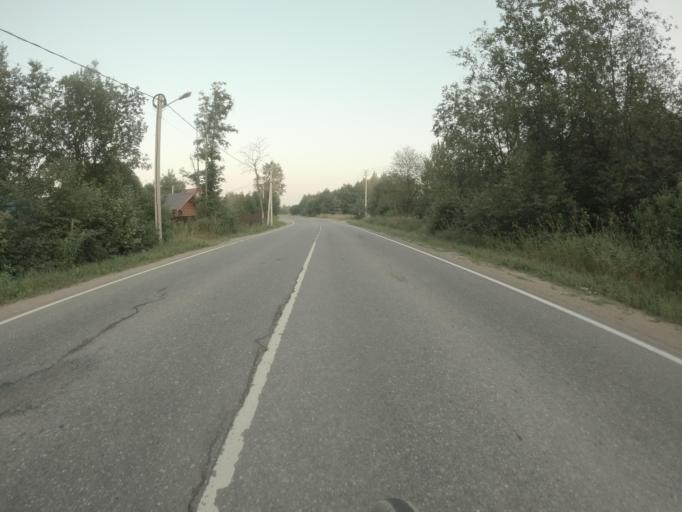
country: RU
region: Leningrad
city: Imeni Sverdlova
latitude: 59.7879
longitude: 30.7200
